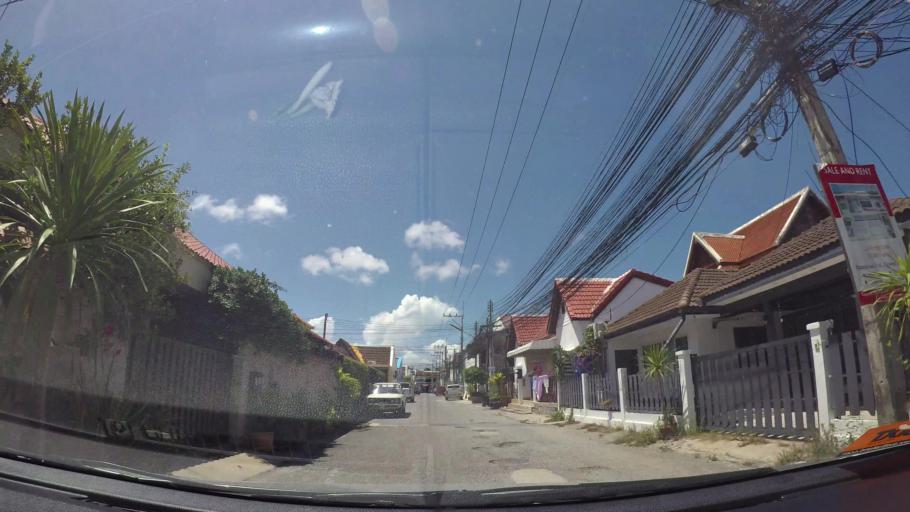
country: TH
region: Chon Buri
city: Phatthaya
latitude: 12.9258
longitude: 100.8857
